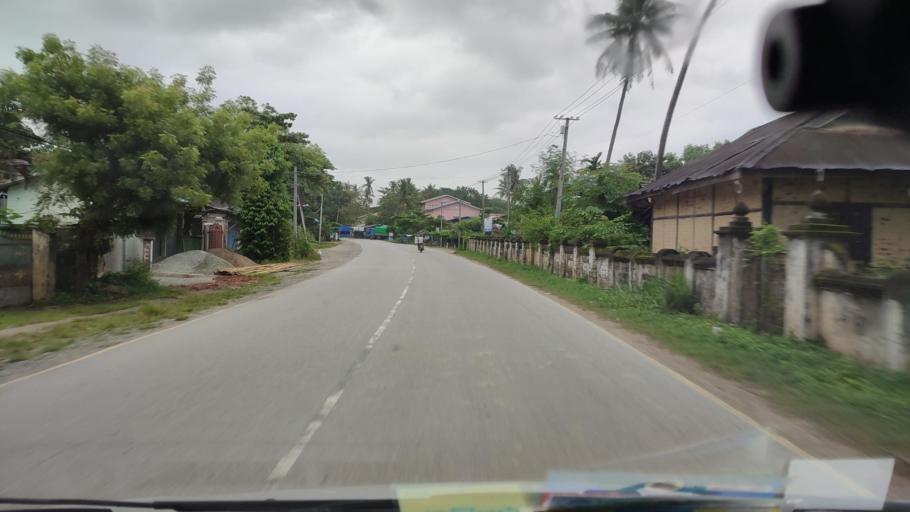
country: MM
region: Bago
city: Taungoo
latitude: 18.9460
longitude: 96.4583
